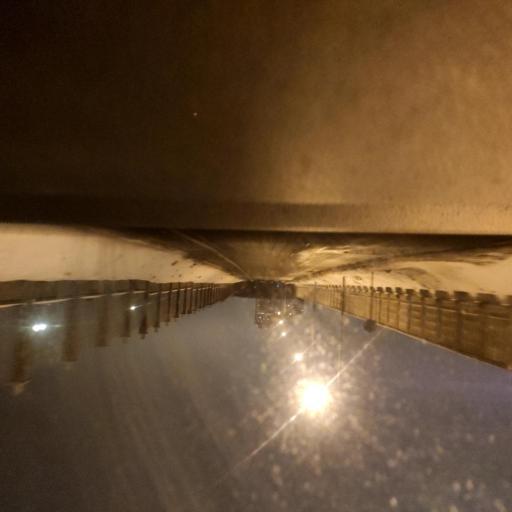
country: RU
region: Moskovskaya
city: Vostryakovo
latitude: 55.6591
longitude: 37.4540
